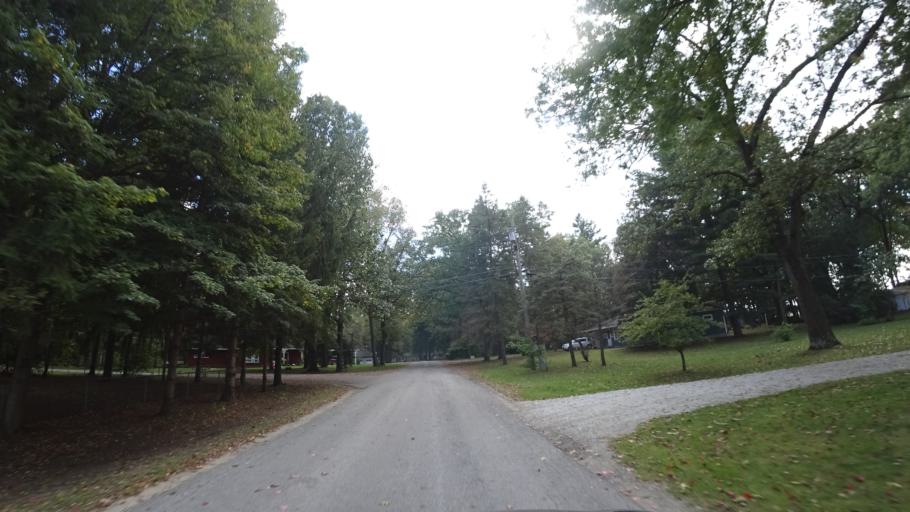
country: US
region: Michigan
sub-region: Saint Joseph County
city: Three Rivers
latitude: 41.9546
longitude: -85.5897
